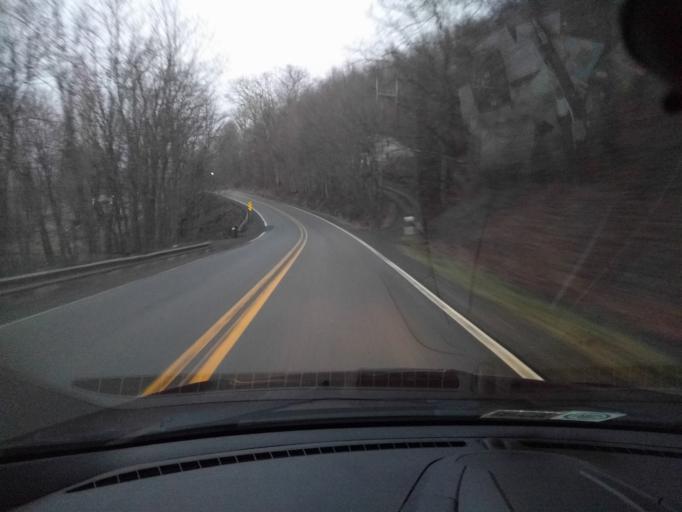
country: US
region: West Virginia
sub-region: Greenbrier County
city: Rainelle
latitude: 37.9779
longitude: -80.8238
